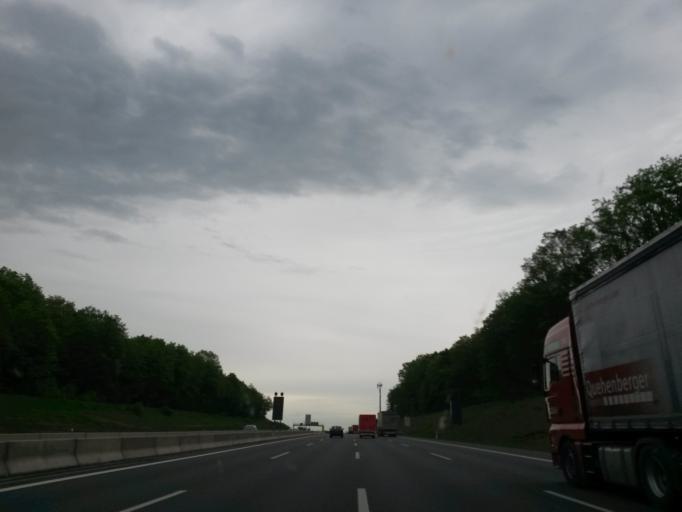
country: DE
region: Bavaria
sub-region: Regierungsbezirk Unterfranken
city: Theilheim
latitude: 49.7457
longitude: 10.0295
